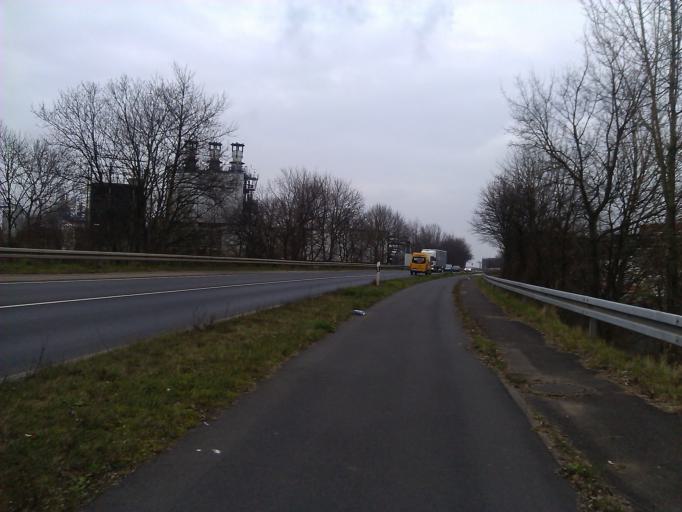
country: DE
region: North Rhine-Westphalia
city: Wesseling
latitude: 50.8332
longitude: 6.9730
